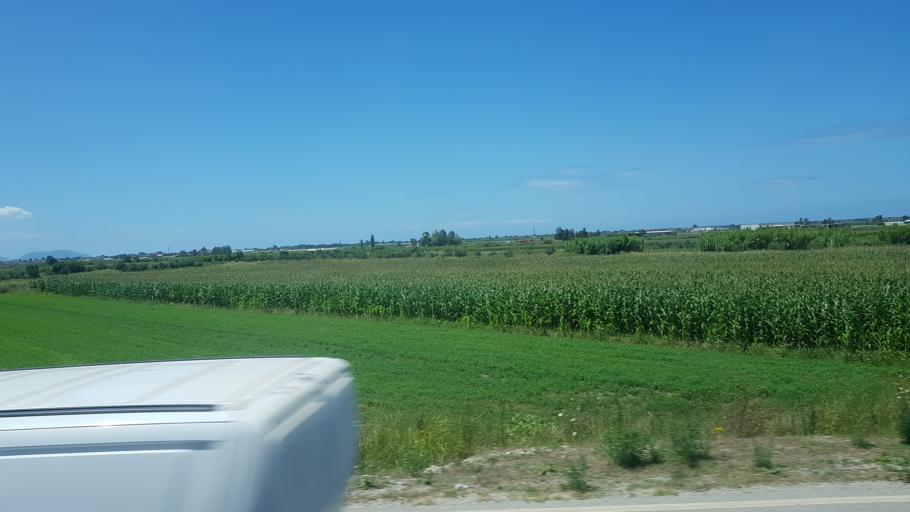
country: AL
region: Fier
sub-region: Rrethi i Fierit
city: Levan
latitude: 40.6641
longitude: 19.4882
